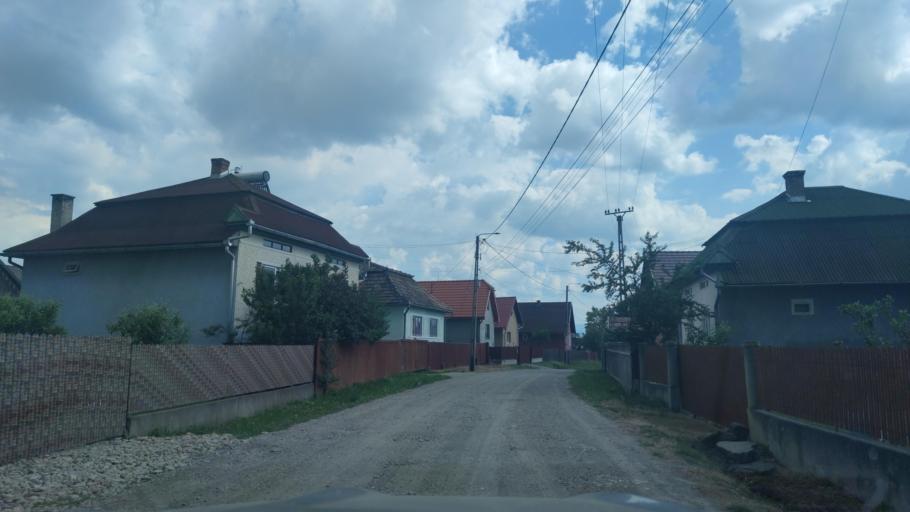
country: RO
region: Harghita
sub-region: Comuna Remetea
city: Remetea
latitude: 46.7979
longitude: 25.4438
